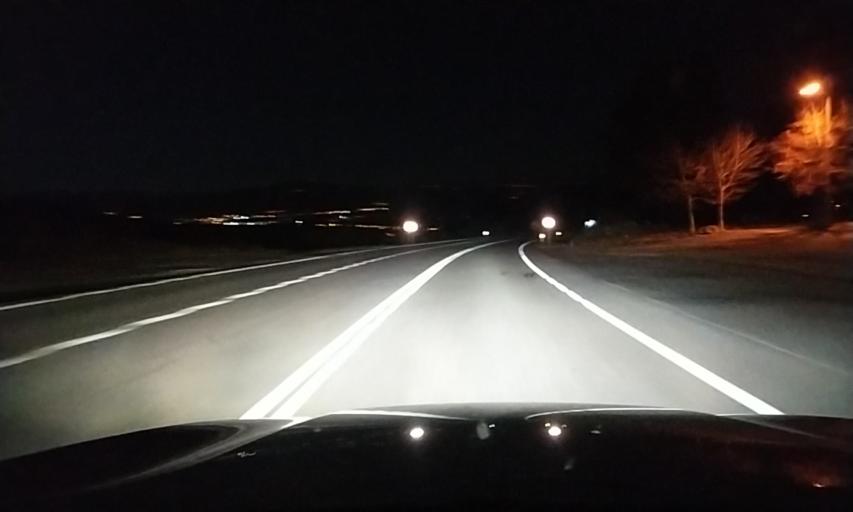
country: ES
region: Galicia
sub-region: Provincia de Ourense
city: Cualedro
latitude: 41.9761
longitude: -7.5210
